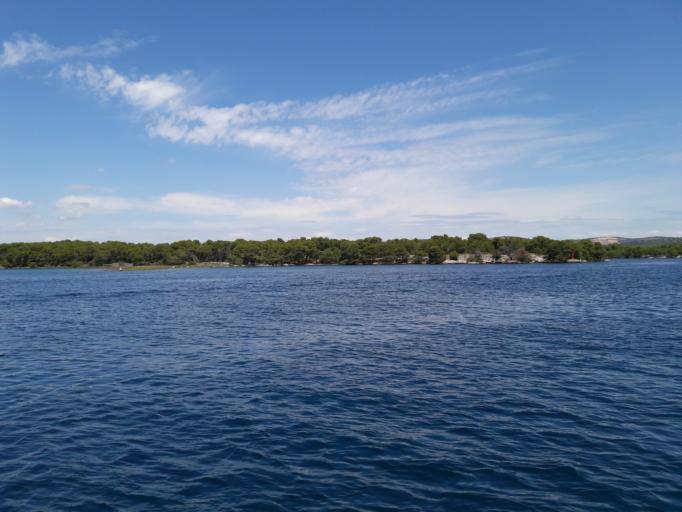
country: HR
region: Sibensko-Kniniska
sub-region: Grad Sibenik
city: Sibenik
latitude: 43.7227
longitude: 15.8544
